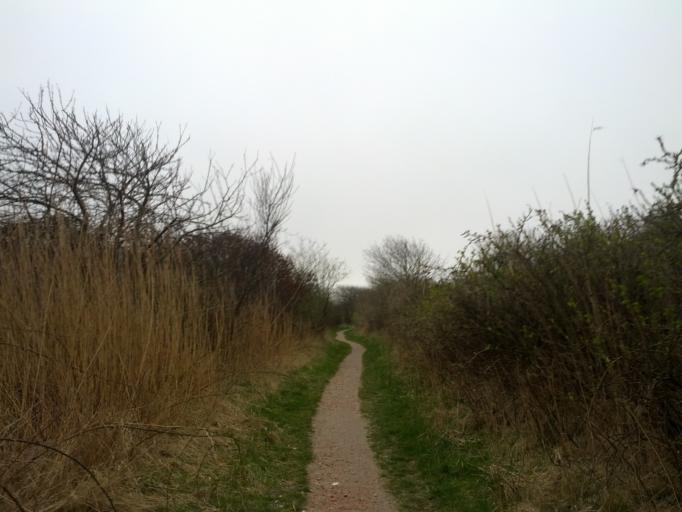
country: DE
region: Lower Saxony
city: Langeoog
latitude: 53.7391
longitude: 7.4715
